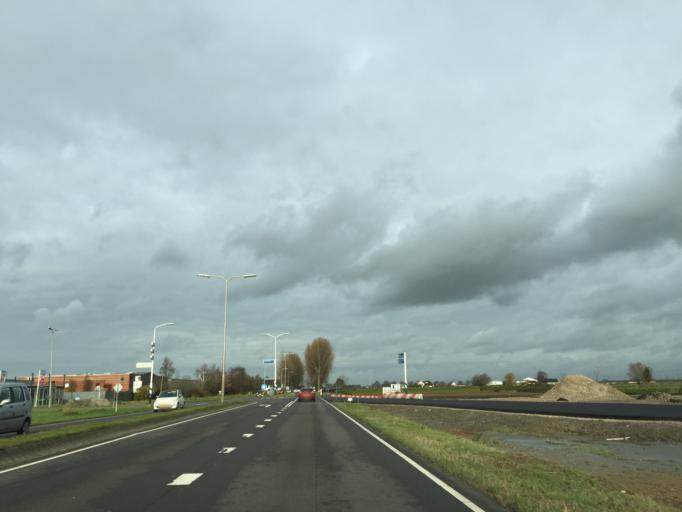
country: NL
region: South Holland
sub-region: Gemeente Rijnwoude
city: Benthuizen
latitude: 52.0732
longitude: 4.5591
